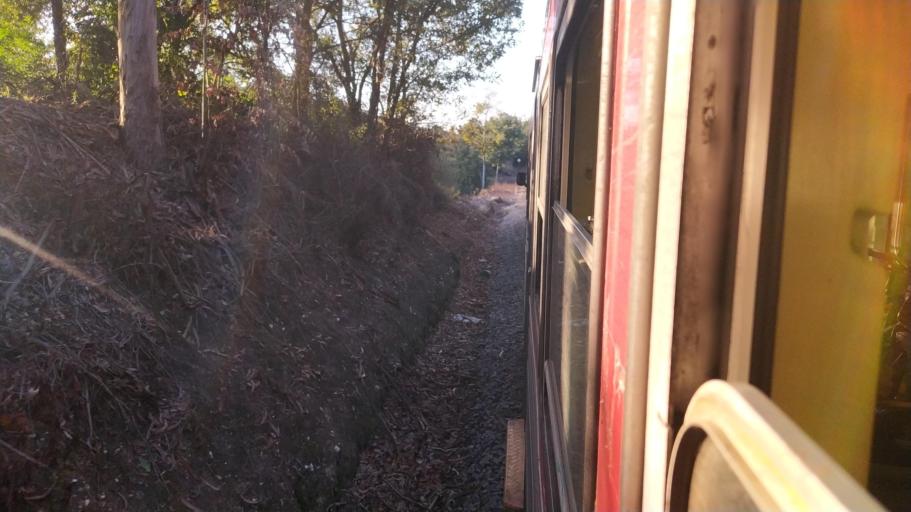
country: PT
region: Aveiro
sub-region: Aveiro
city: Eixo
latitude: 40.6339
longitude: -8.5753
